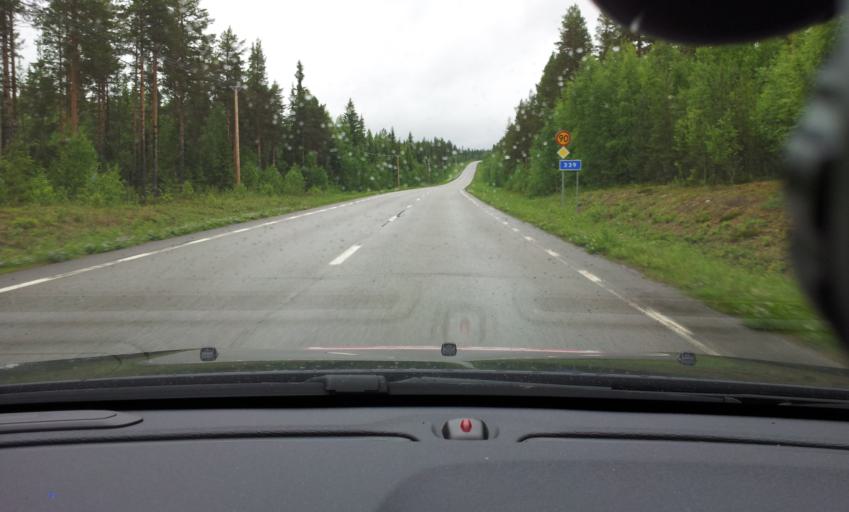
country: SE
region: Jaemtland
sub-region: Krokoms Kommun
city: Krokom
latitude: 63.4592
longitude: 14.4912
